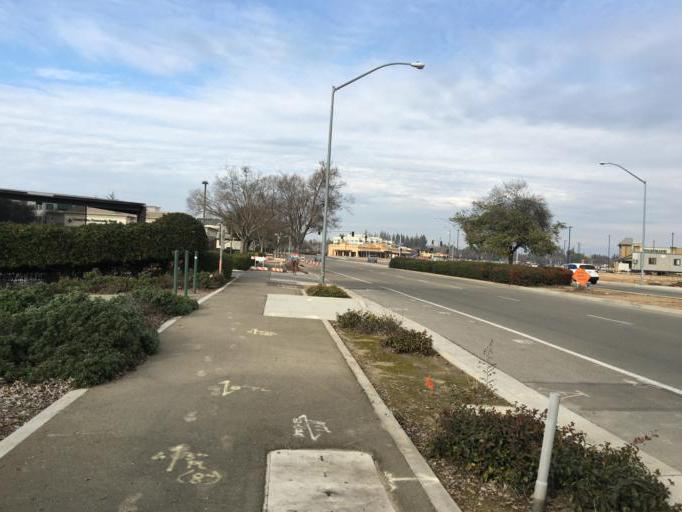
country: US
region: California
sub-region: Fresno County
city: Clovis
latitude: 36.8541
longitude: -119.7841
